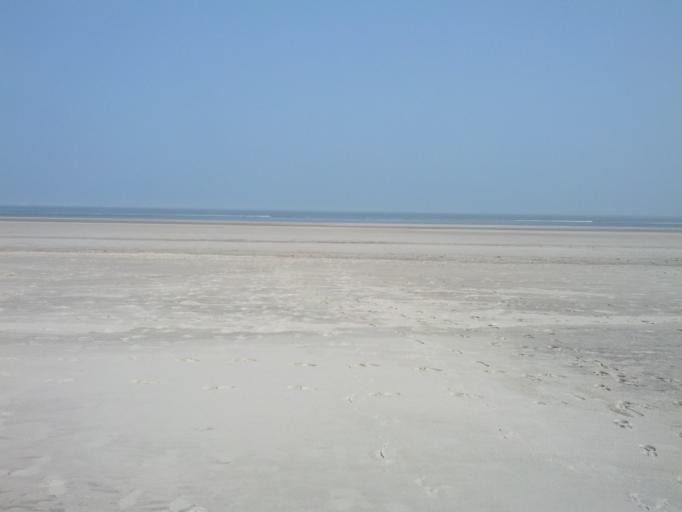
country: DE
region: Lower Saxony
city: Spiekeroog
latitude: 53.7588
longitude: 7.5907
